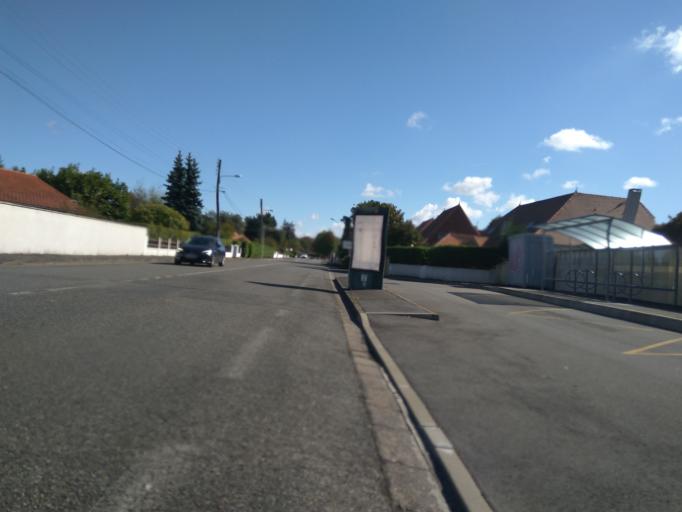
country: FR
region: Aquitaine
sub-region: Departement des Pyrenees-Atlantiques
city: Idron
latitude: 43.2990
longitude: -0.3207
